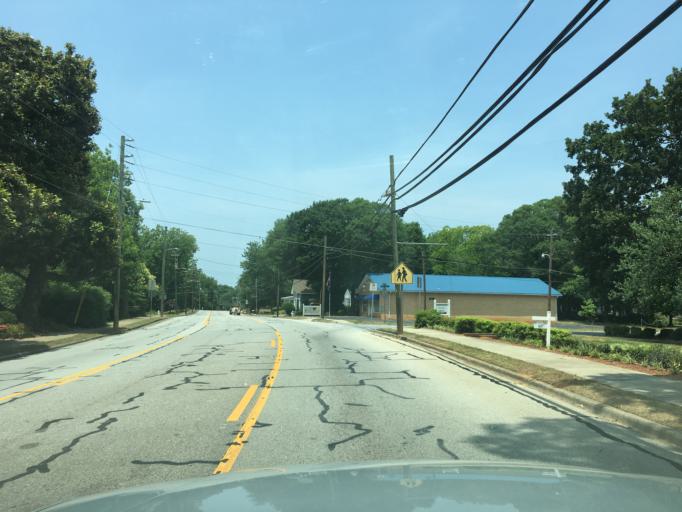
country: US
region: Georgia
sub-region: Hart County
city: Hartwell
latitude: 34.3468
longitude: -82.9272
